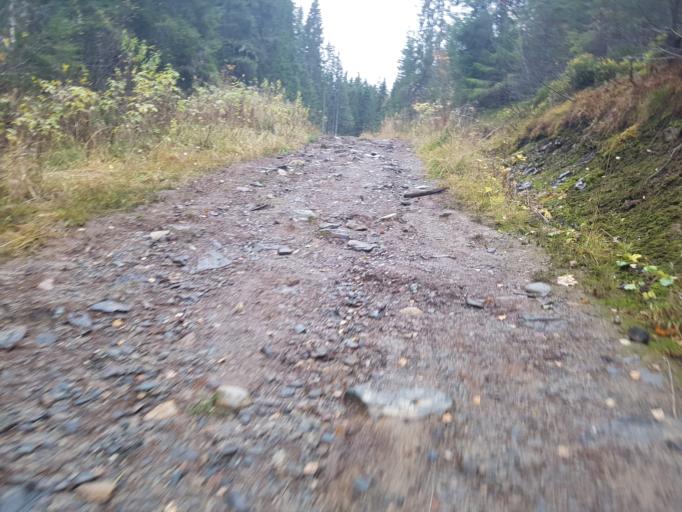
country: NO
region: Sor-Trondelag
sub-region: Melhus
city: Melhus
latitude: 63.3861
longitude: 10.2424
